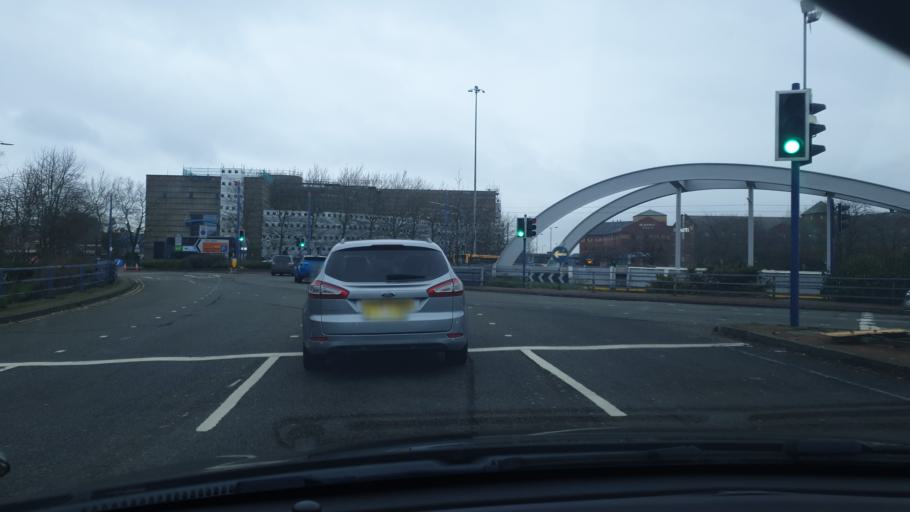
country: GB
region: England
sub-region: Wolverhampton
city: Wolverhampton
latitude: 52.5831
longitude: -2.1219
